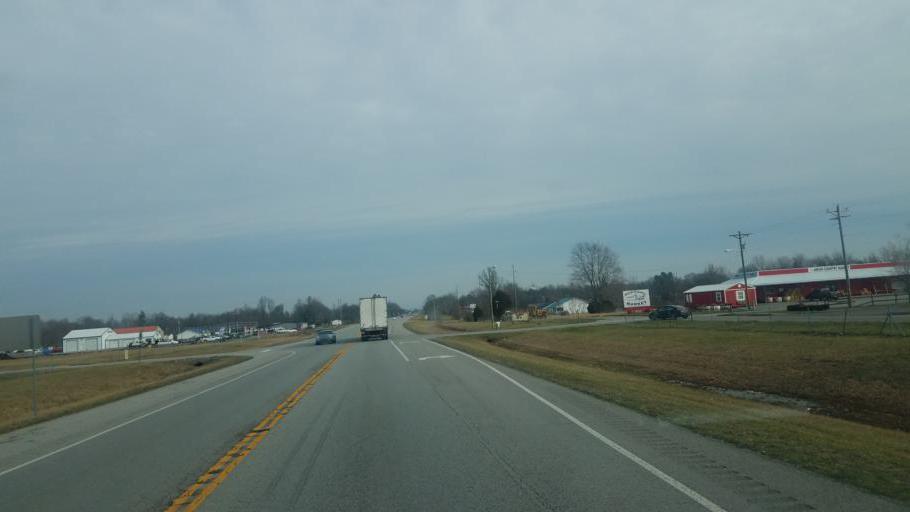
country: US
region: Kentucky
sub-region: Boyle County
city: Junction City
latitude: 37.5771
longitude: -84.7908
